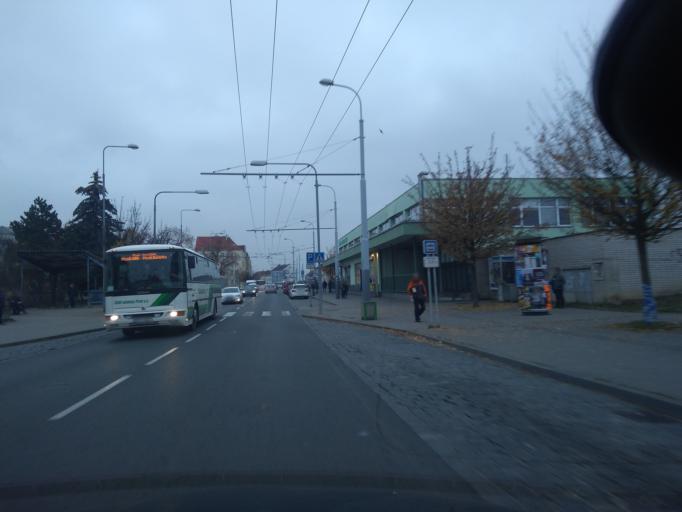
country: CZ
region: Plzensky
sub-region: Okres Plzen-Mesto
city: Pilsen
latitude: 49.7461
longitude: 13.3639
